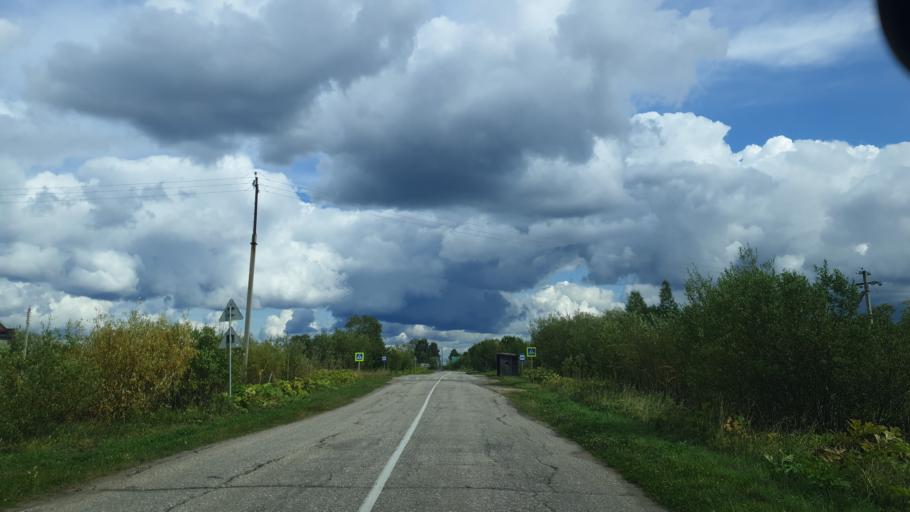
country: RU
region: Komi Republic
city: Aykino
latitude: 61.9521
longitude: 50.1735
